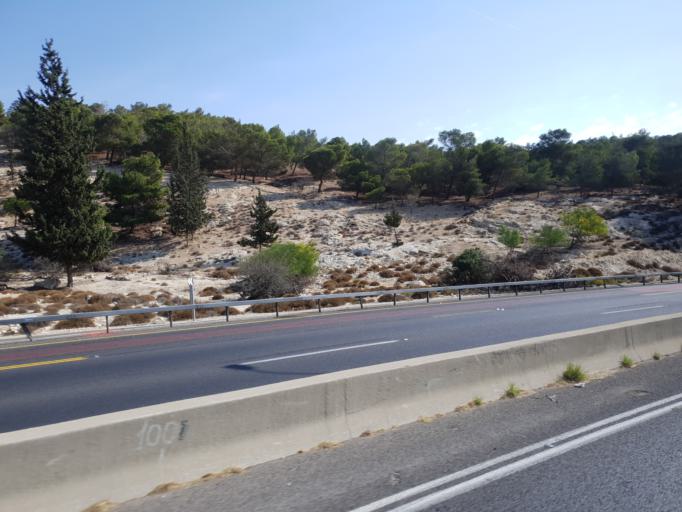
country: PS
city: Az Za`ayyim
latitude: 31.7878
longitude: 35.2791
